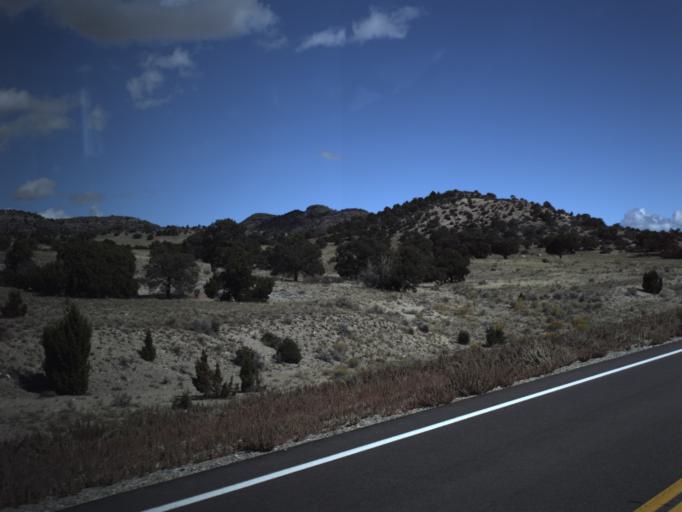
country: US
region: Utah
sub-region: Beaver County
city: Milford
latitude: 38.5174
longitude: -113.5467
